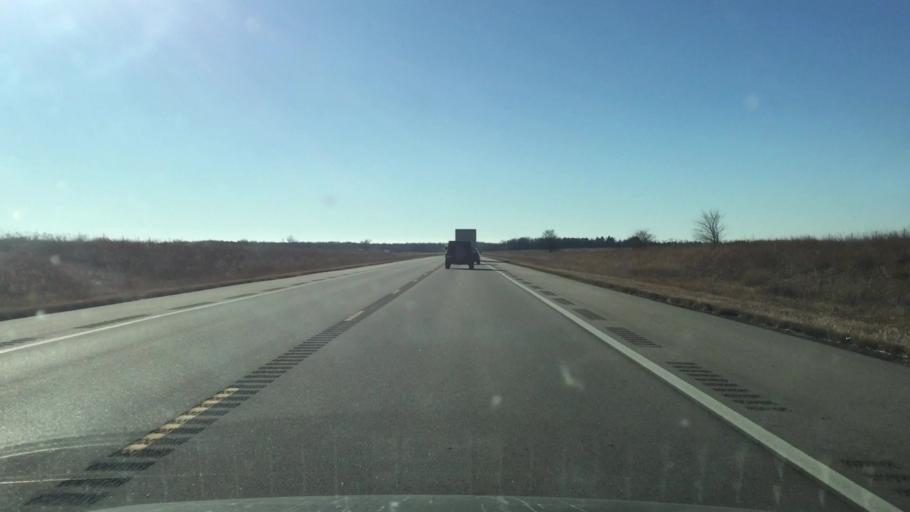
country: US
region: Kansas
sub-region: Allen County
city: Iola
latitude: 38.0481
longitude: -95.3805
